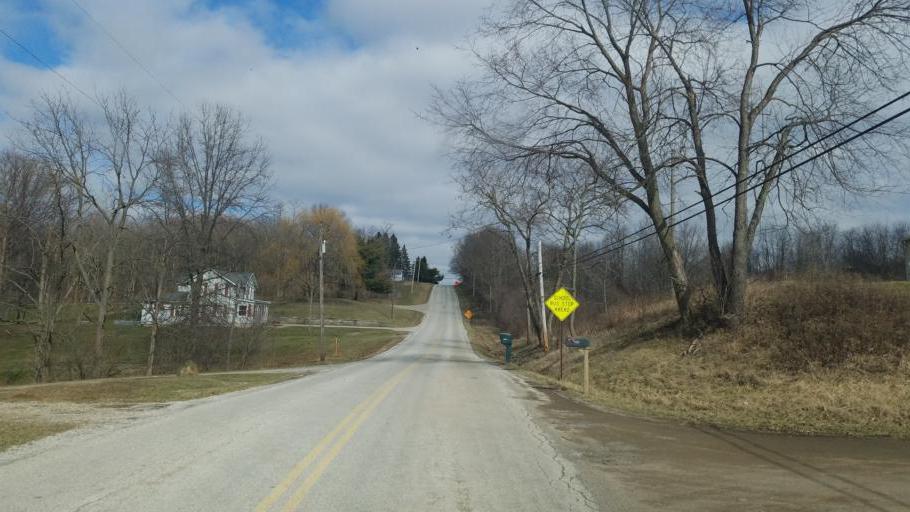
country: US
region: Ohio
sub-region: Sandusky County
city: Bellville
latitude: 40.5715
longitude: -82.5095
